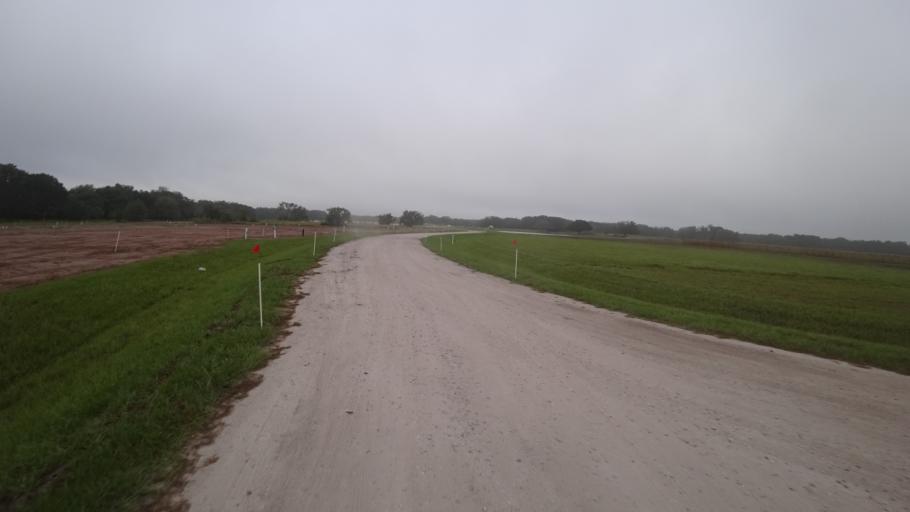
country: US
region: Florida
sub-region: Sarasota County
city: Lake Sarasota
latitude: 27.2904
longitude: -82.2168
